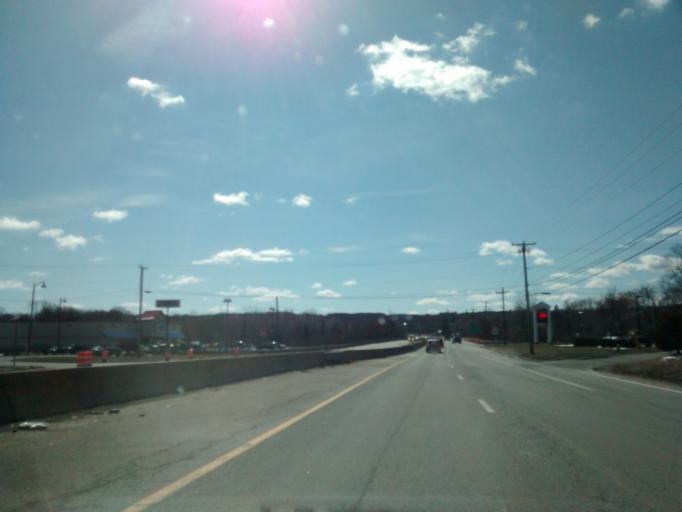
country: US
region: Massachusetts
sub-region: Worcester County
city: Millbury
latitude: 42.1929
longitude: -71.7709
